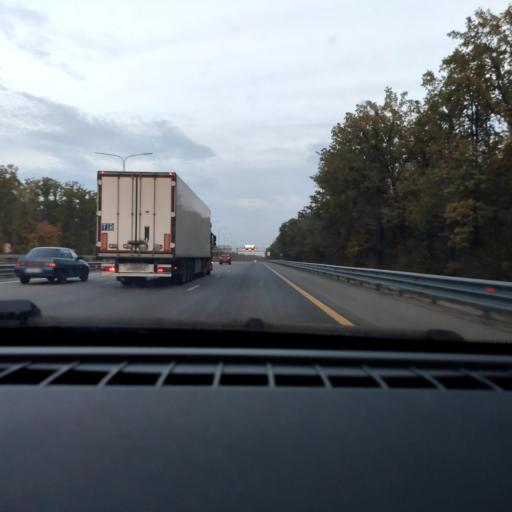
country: RU
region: Voronezj
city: Podgornoye
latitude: 51.8352
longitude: 39.2288
